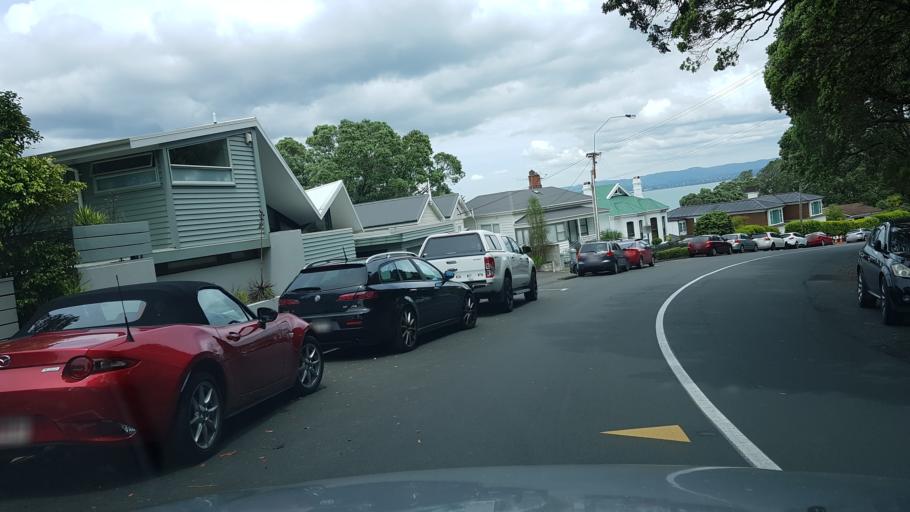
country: NZ
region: Auckland
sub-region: Auckland
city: North Shore
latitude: -36.8210
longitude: 174.7370
